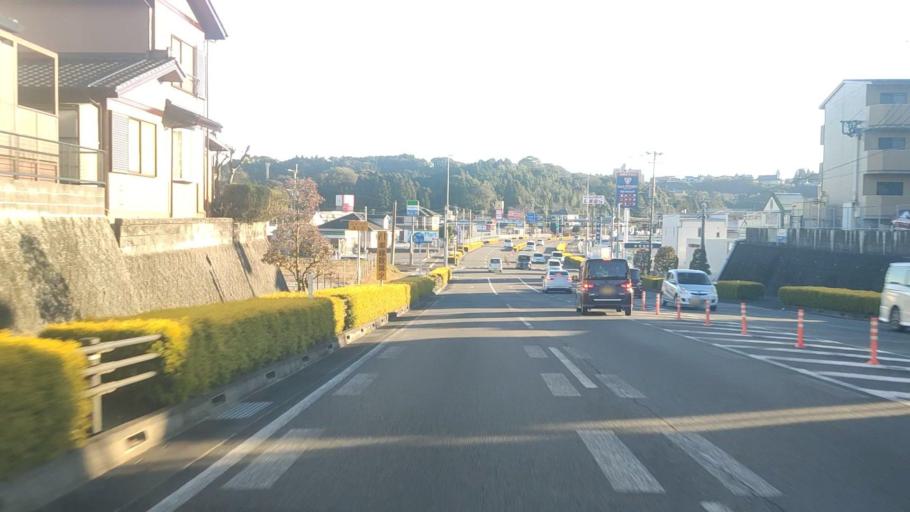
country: JP
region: Miyazaki
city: Miyazaki-shi
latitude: 31.8733
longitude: 131.3925
